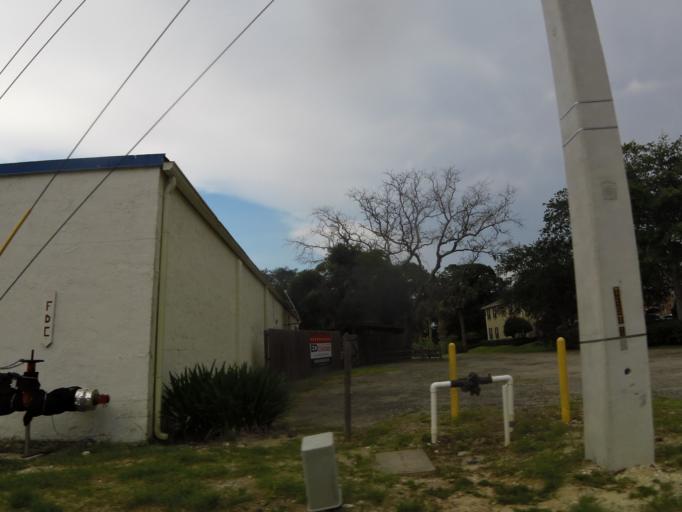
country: US
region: Florida
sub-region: Duval County
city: Jacksonville Beach
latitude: 30.2876
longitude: -81.4070
